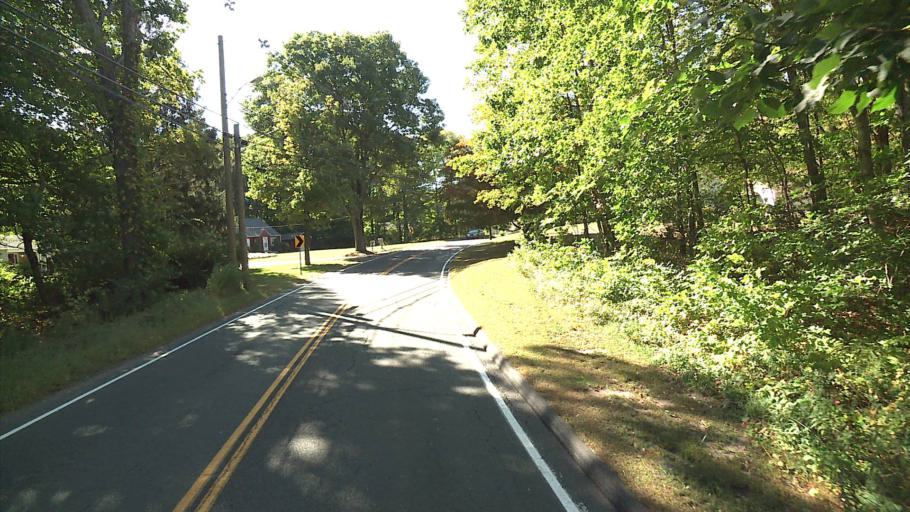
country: US
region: Connecticut
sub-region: Hartford County
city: Bristol
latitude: 41.7116
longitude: -72.9452
